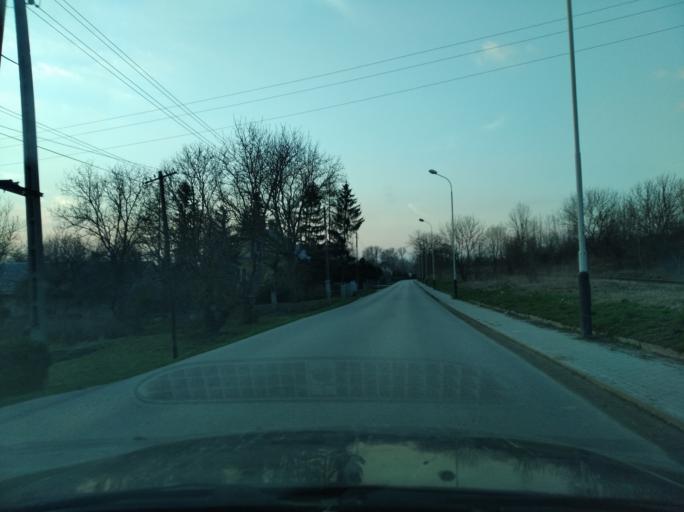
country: PL
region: Subcarpathian Voivodeship
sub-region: Powiat przeworski
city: Przeworsk
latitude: 50.0440
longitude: 22.5042
